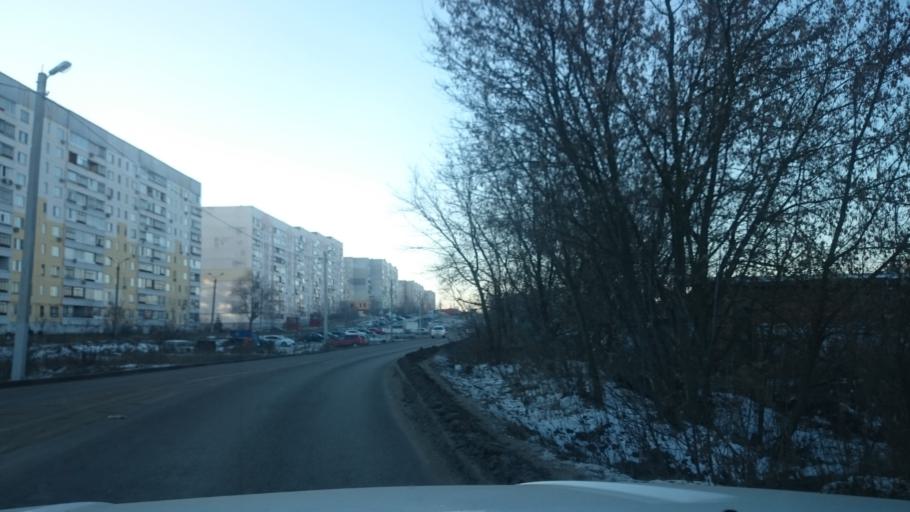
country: RU
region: Tula
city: Tula
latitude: 54.2073
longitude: 37.6426
